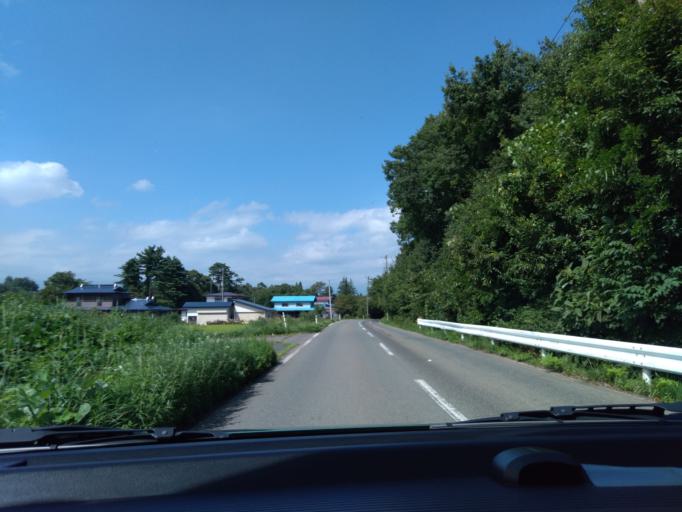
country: JP
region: Iwate
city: Shizukuishi
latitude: 39.6555
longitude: 140.9923
